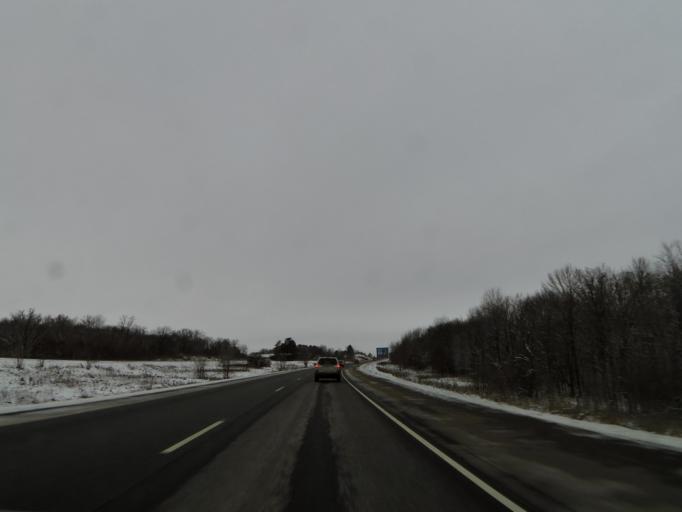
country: US
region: Wisconsin
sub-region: Saint Croix County
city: Baldwin
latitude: 44.9379
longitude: -92.3439
